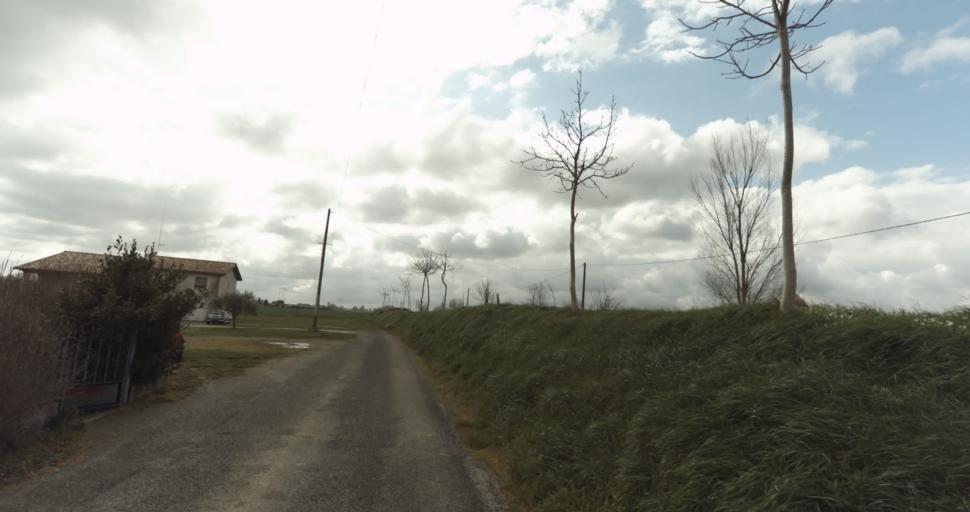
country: FR
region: Midi-Pyrenees
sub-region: Departement de la Haute-Garonne
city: Auterive
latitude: 43.3421
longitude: 1.4488
